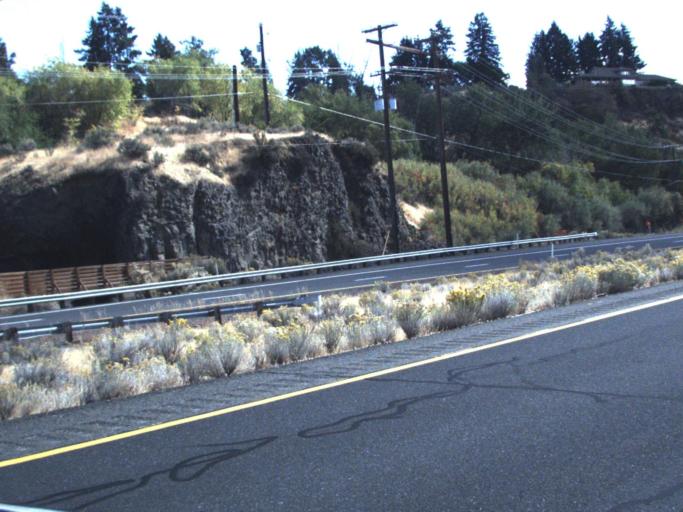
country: US
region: Washington
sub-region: Yakima County
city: Gleed
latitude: 46.6955
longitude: -120.6539
